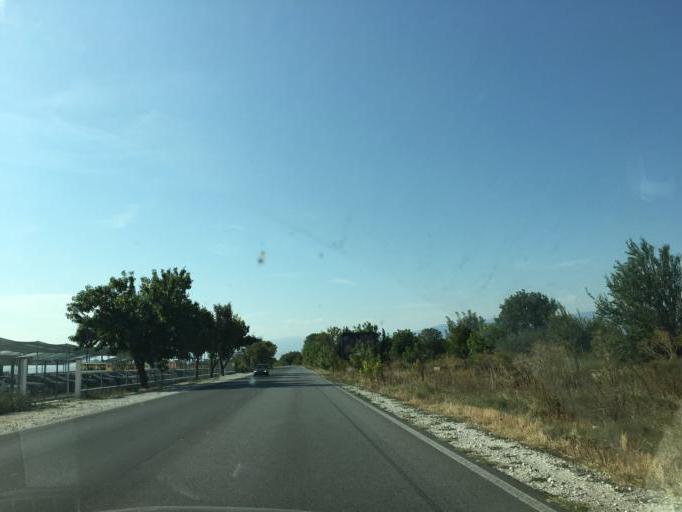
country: BG
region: Pazardzhik
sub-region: Obshtina Pazardzhik
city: Pazardzhik
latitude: 42.2269
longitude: 24.3104
